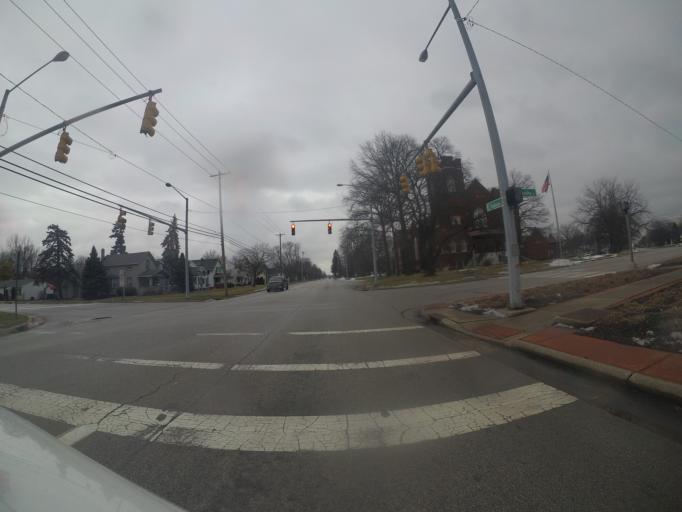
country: US
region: Ohio
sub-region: Wood County
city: Perrysburg
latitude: 41.5586
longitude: -83.6238
